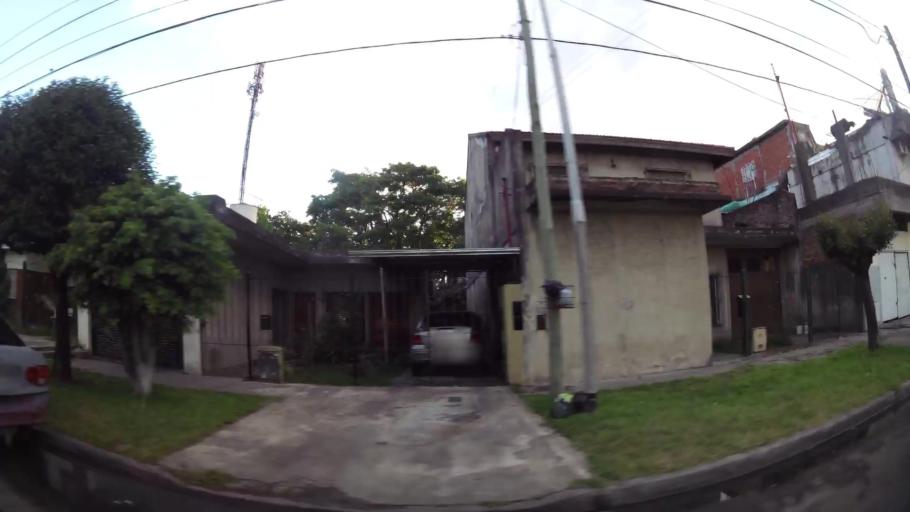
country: AR
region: Buenos Aires
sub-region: Partido de Avellaneda
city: Avellaneda
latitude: -34.7045
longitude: -58.3417
